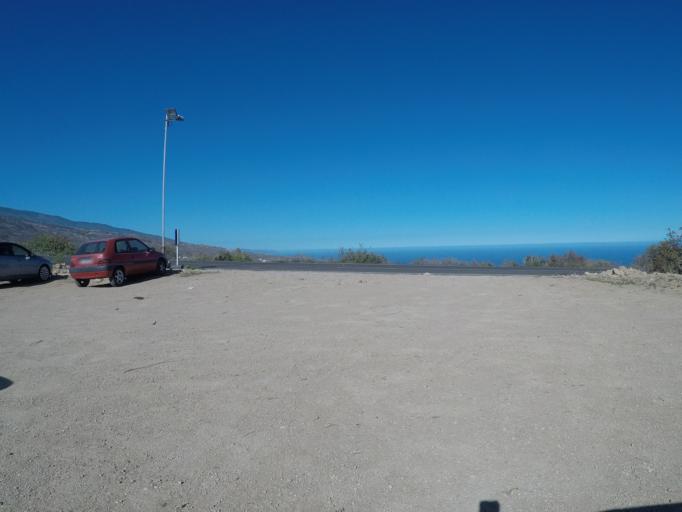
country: ES
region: Canary Islands
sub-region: Provincia de Santa Cruz de Tenerife
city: Fasnia
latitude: 28.2292
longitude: -16.5000
